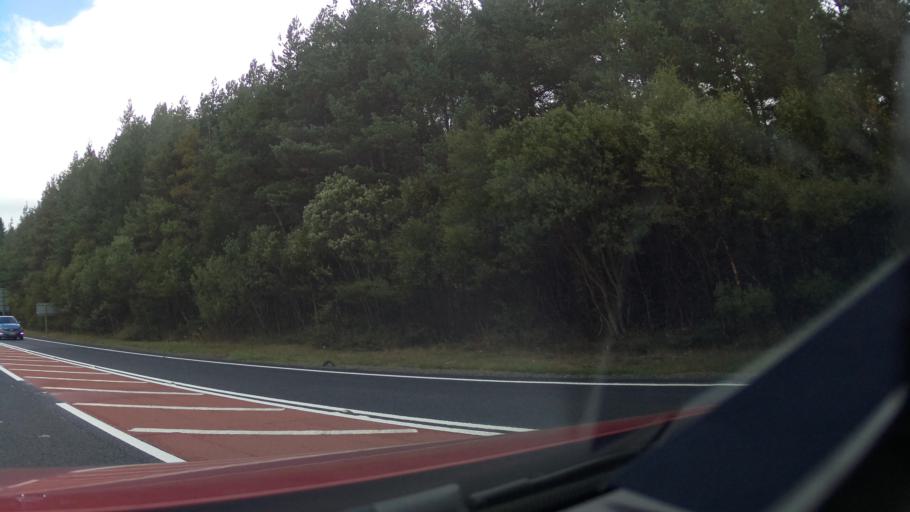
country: GB
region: Scotland
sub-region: Highland
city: Inverness
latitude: 57.3804
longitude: -4.0515
